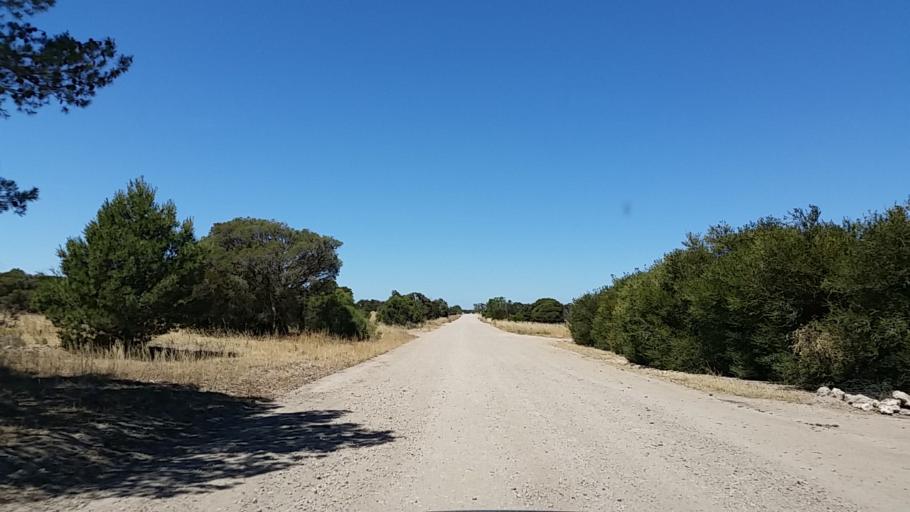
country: AU
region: South Australia
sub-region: Yorke Peninsula
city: Honiton
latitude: -35.0720
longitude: 137.5226
